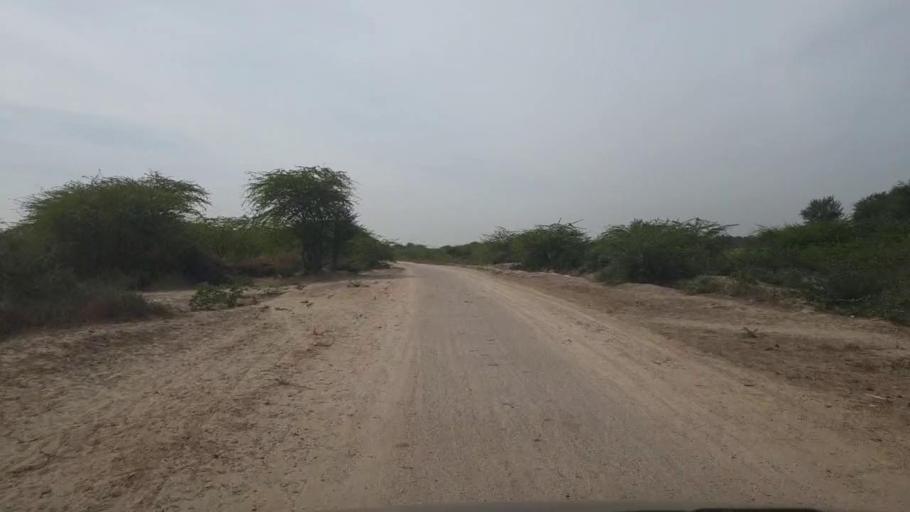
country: PK
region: Sindh
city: Umarkot
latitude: 25.2495
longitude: 69.7189
